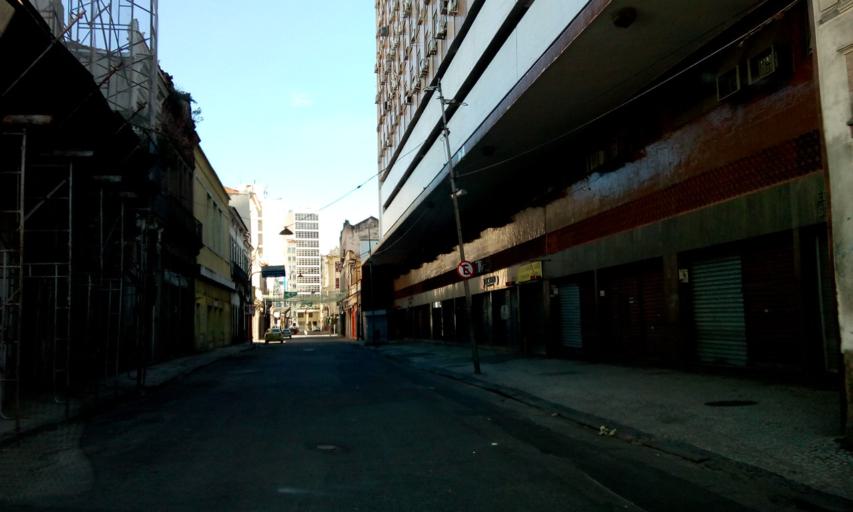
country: BR
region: Rio de Janeiro
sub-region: Rio De Janeiro
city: Rio de Janeiro
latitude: -22.9058
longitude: -43.1860
